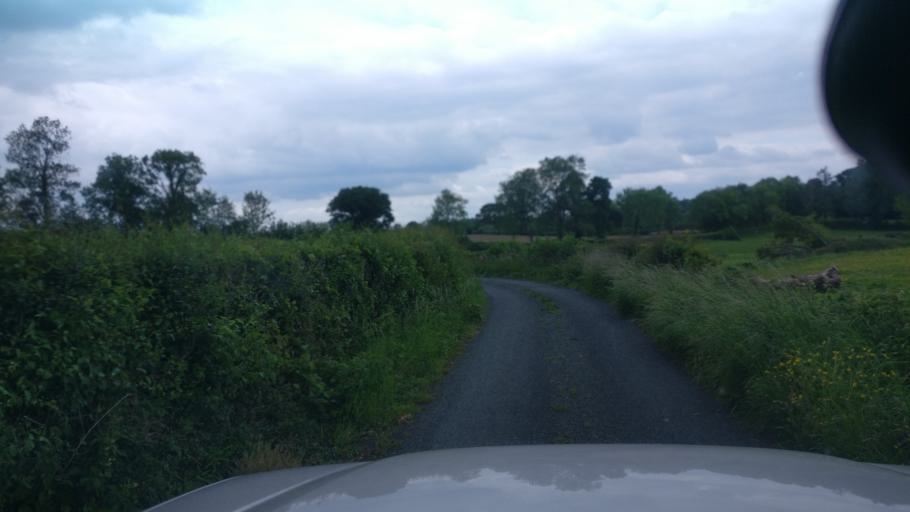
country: IE
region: Connaught
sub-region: County Galway
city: Ballinasloe
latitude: 53.3087
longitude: -8.2580
